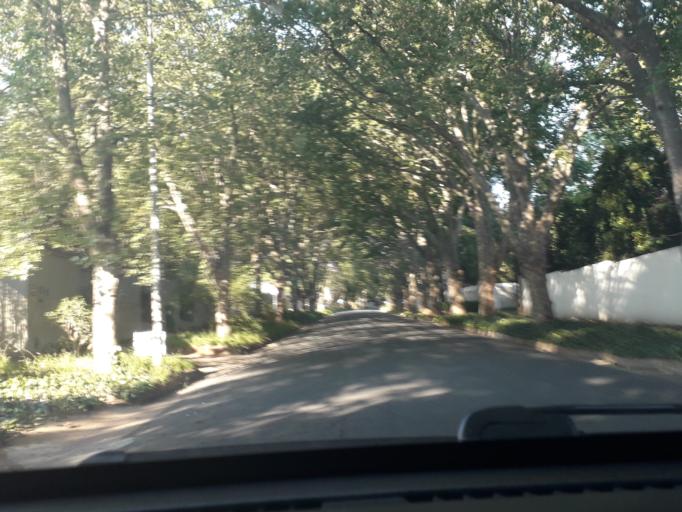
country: ZA
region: Gauteng
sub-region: City of Johannesburg Metropolitan Municipality
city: Johannesburg
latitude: -26.1583
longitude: 28.0375
